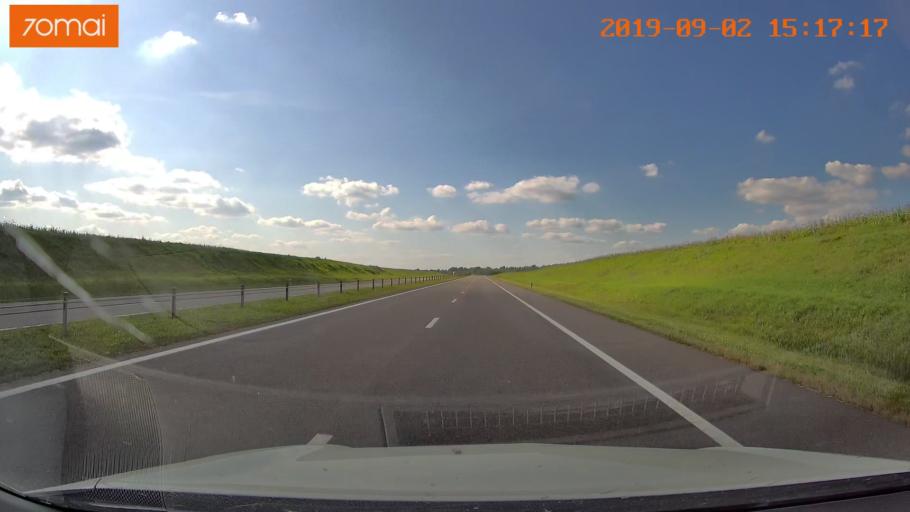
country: BY
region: Mogilev
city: Byalynichy
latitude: 53.9407
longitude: 29.5988
